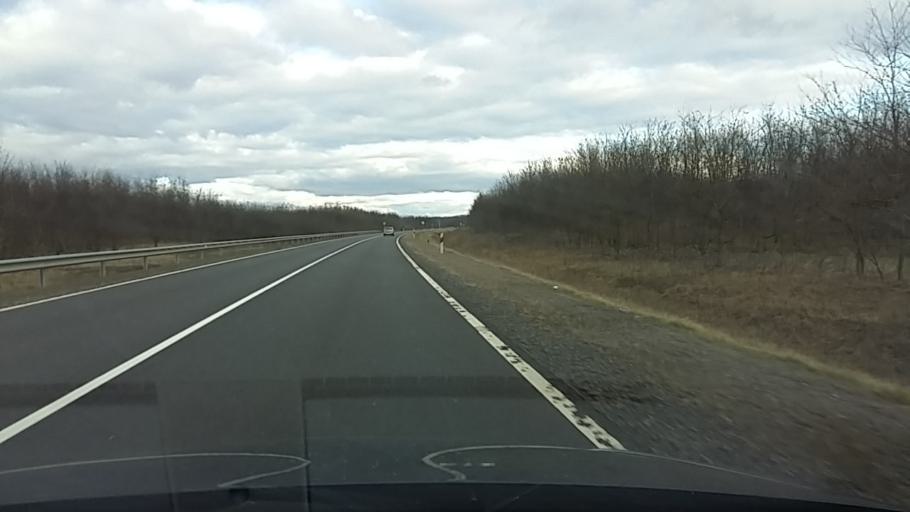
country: HU
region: Szabolcs-Szatmar-Bereg
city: Nyirpazony
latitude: 47.9925
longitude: 21.8245
